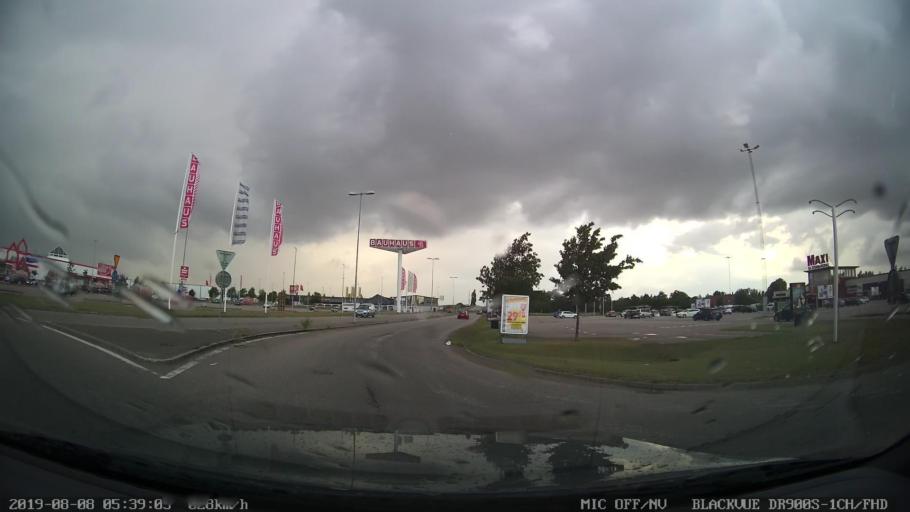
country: SE
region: Skane
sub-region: Helsingborg
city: Hyllinge
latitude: 56.0997
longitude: 12.8581
